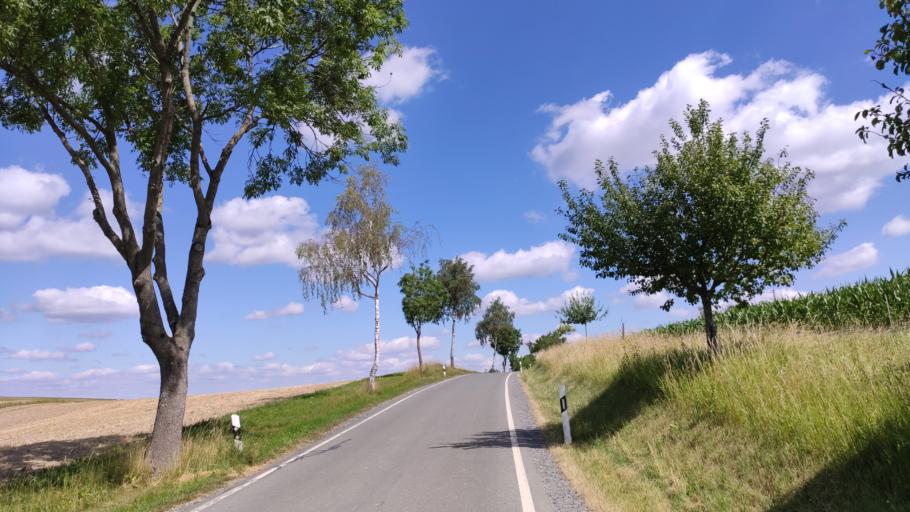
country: DE
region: Bavaria
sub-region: Upper Franconia
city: Ludwigsstadt
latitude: 50.5032
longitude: 11.4176
